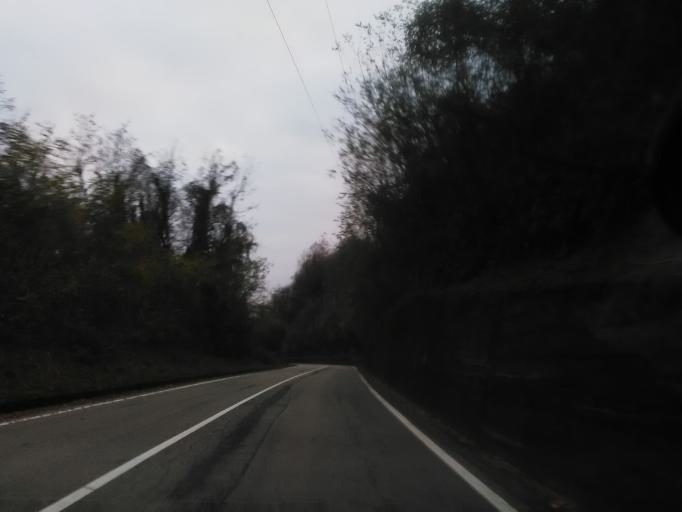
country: IT
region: Piedmont
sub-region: Provincia di Vercelli
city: Quarona
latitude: 45.7781
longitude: 8.2596
